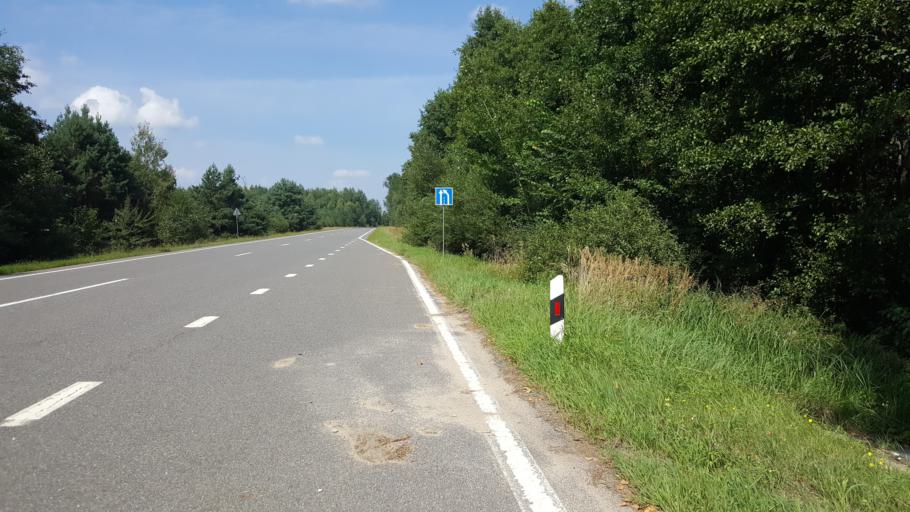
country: BY
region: Brest
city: Kamyanyuki
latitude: 52.5515
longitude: 23.6440
